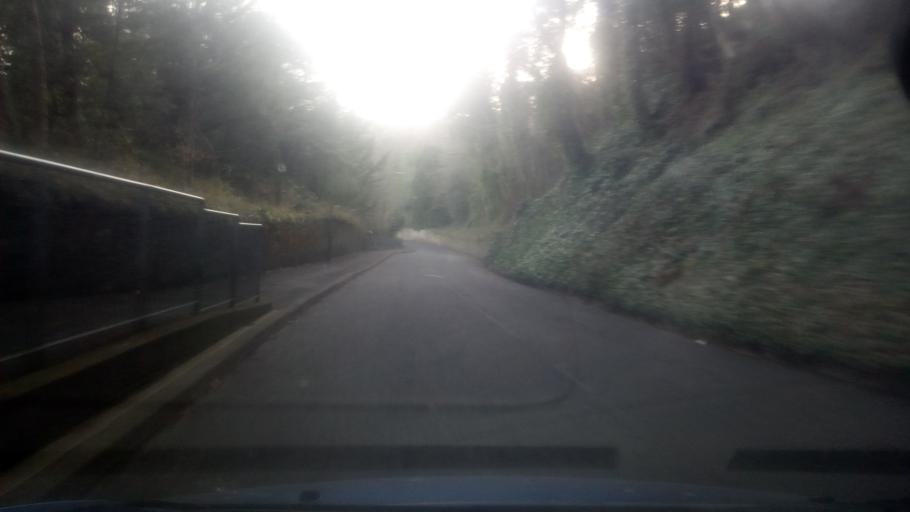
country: GB
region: Scotland
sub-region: The Scottish Borders
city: Jedburgh
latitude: 55.4825
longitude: -2.5539
